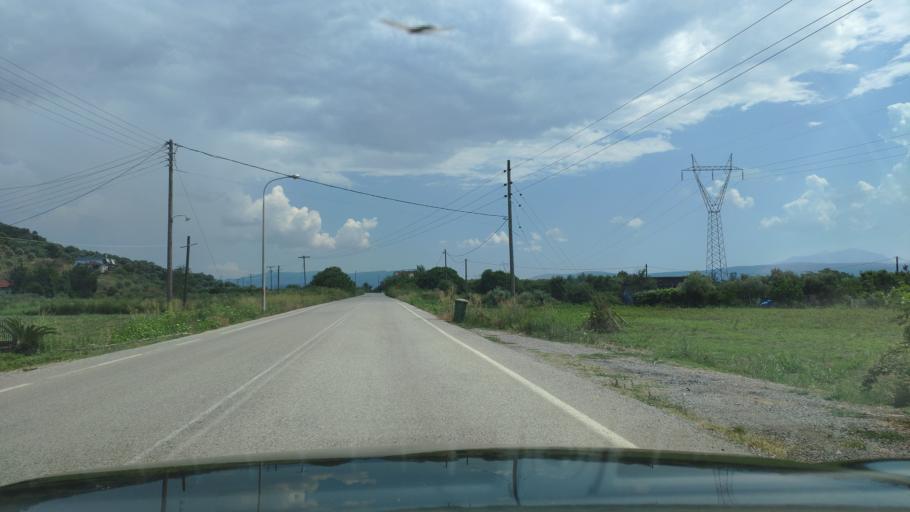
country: GR
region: West Greece
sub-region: Nomos Aitolias kai Akarnanias
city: Krikellos
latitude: 38.9694
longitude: 21.1680
